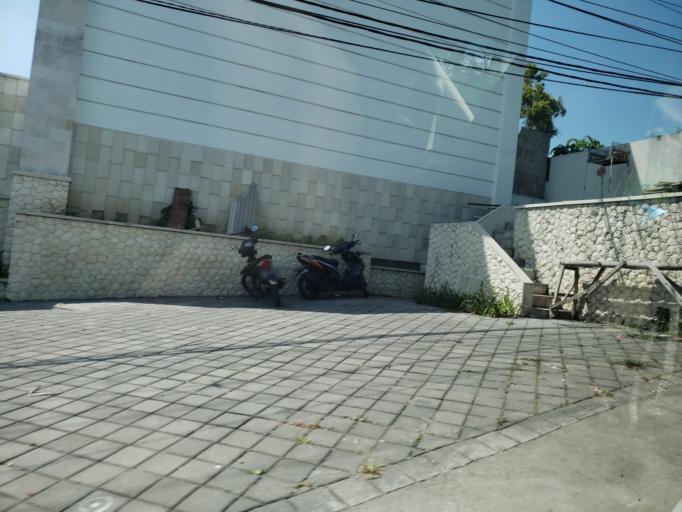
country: ID
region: Bali
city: Kangin
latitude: -8.8279
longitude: 115.1495
